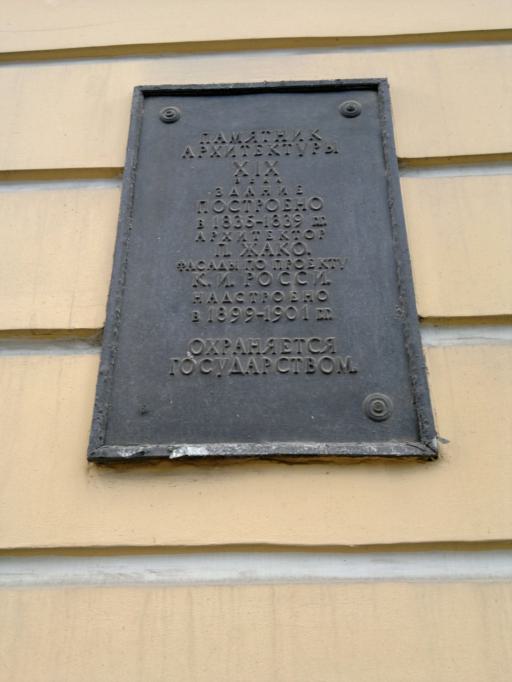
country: RU
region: St.-Petersburg
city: Saint Petersburg
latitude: 59.9365
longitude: 30.3319
